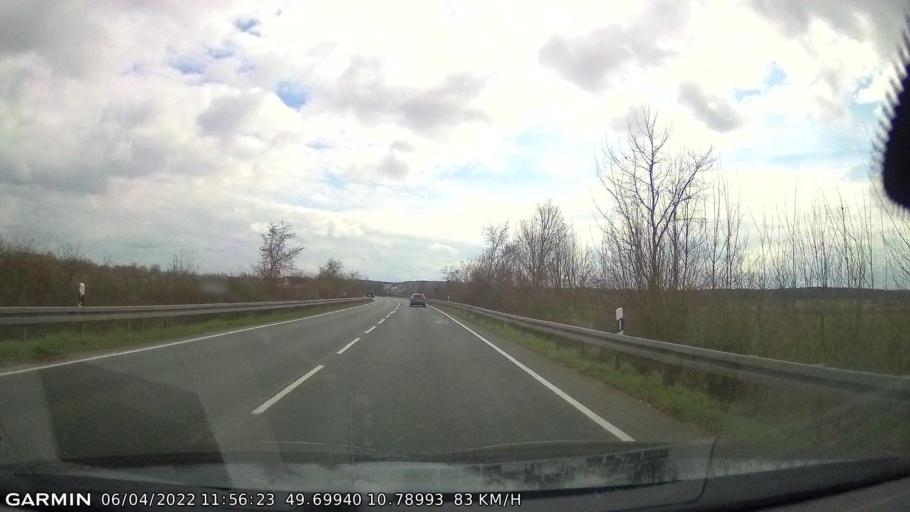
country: DE
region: Bavaria
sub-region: Regierungsbezirk Mittelfranken
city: Lonnerstadt
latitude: 49.6993
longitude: 10.7901
